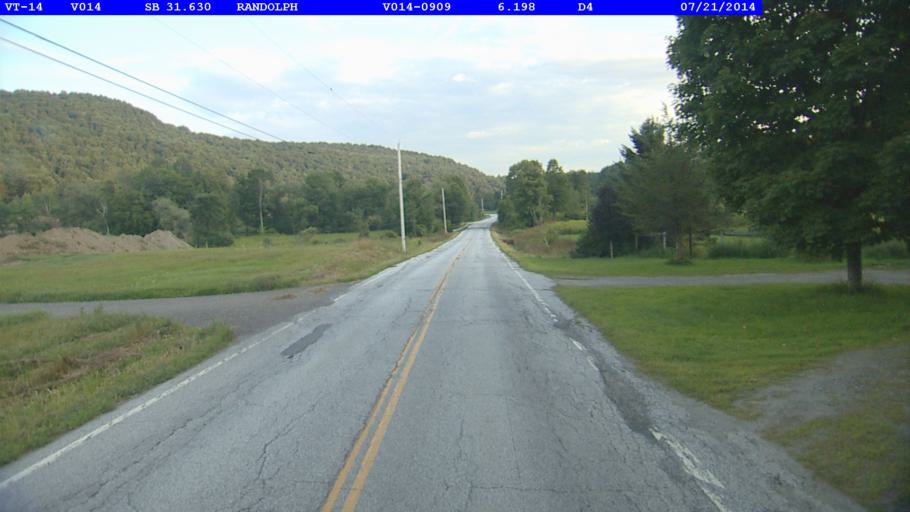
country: US
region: Vermont
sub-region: Orange County
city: Chelsea
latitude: 43.9576
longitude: -72.5510
